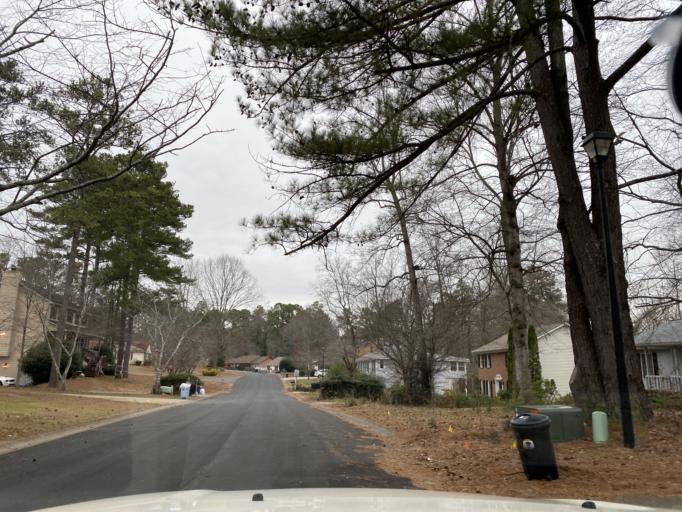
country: US
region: Georgia
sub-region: Cobb County
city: Fair Oaks
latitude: 33.9123
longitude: -84.5672
